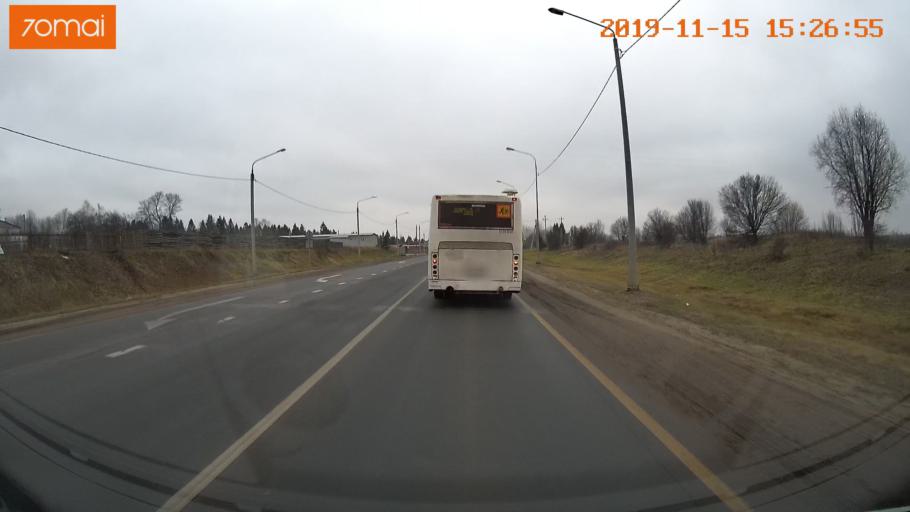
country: RU
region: Jaroslavl
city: Danilov
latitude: 58.1471
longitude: 40.1478
